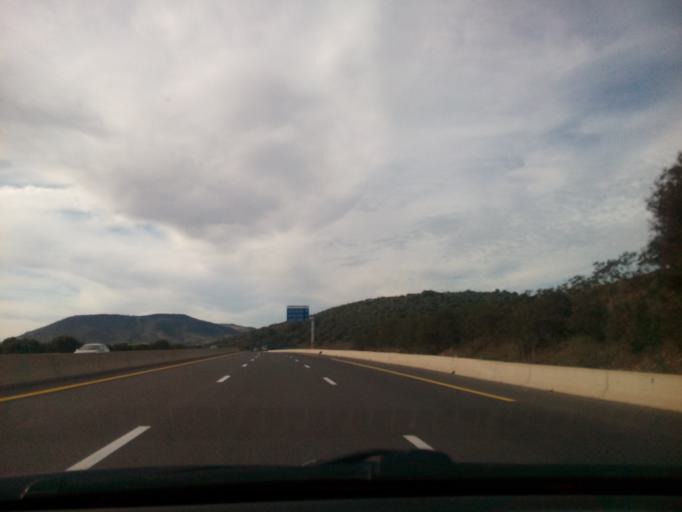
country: DZ
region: Sidi Bel Abbes
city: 'Ain el Berd
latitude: 35.4216
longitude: -0.4738
